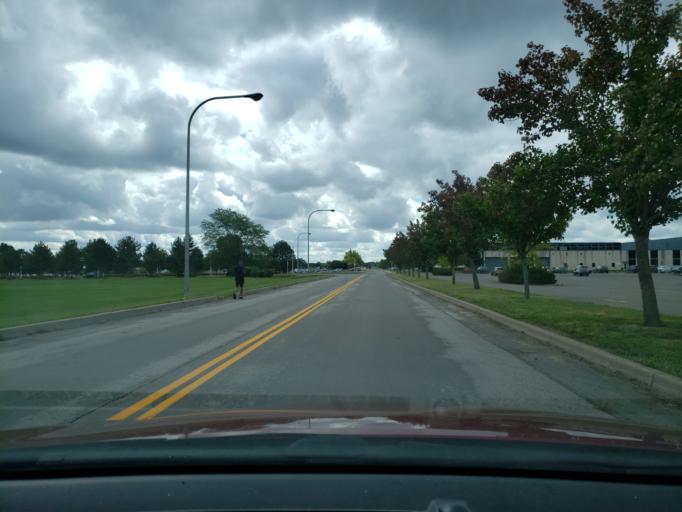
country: US
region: New York
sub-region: Monroe County
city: North Gates
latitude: 43.1560
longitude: -77.7345
